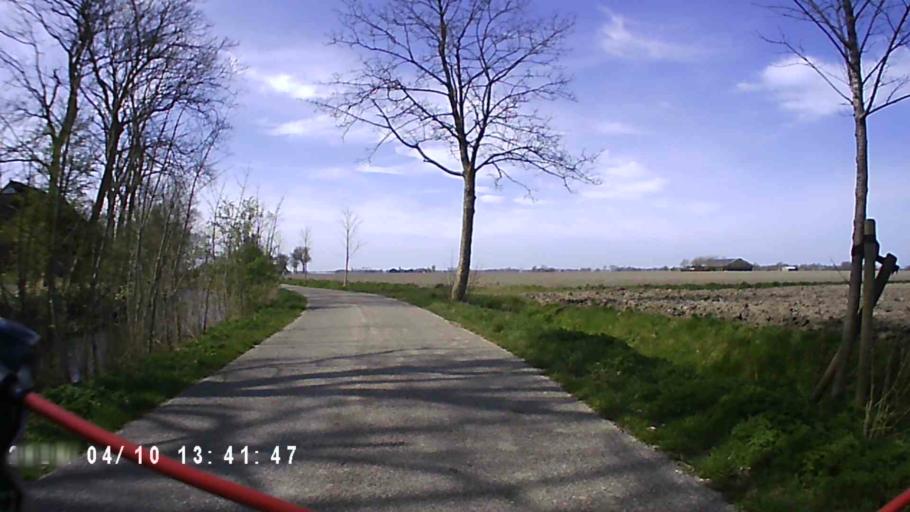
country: NL
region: Groningen
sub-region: Gemeente De Marne
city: Ulrum
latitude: 53.3746
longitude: 6.3828
